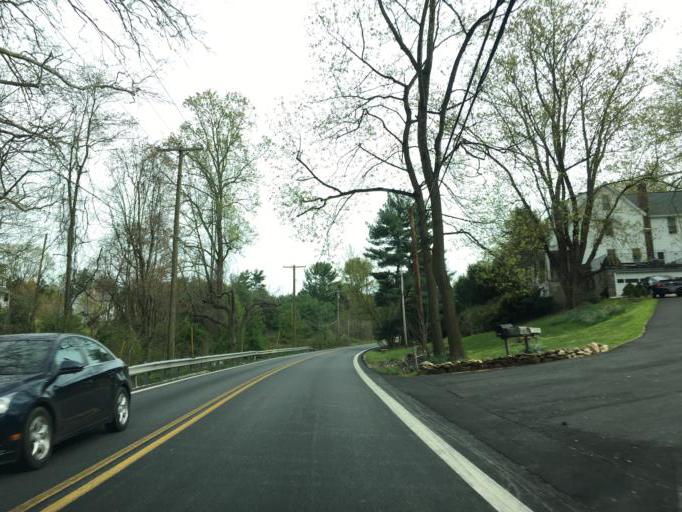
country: US
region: Maryland
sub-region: Baltimore County
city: Hunt Valley
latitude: 39.4947
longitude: -76.5679
